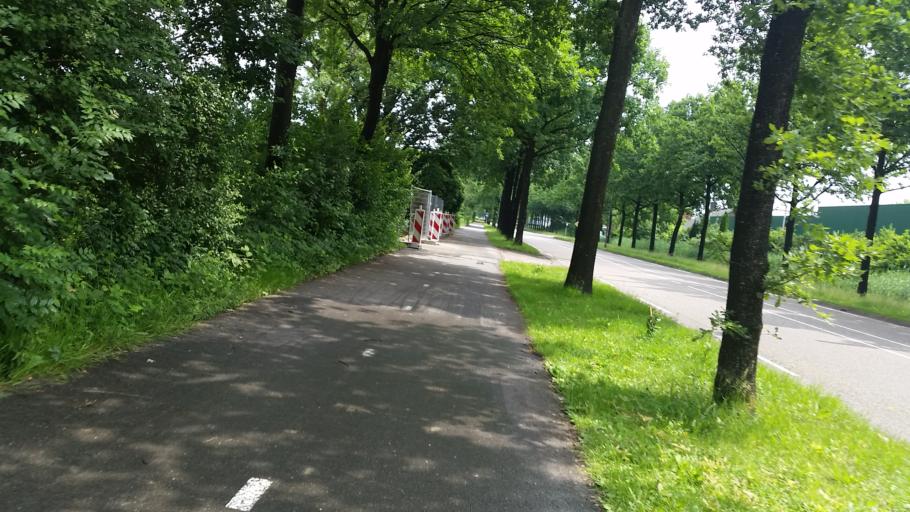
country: NL
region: Gelderland
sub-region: Gemeente Geldermalsen
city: Geldermalsen
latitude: 51.8764
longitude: 5.3006
